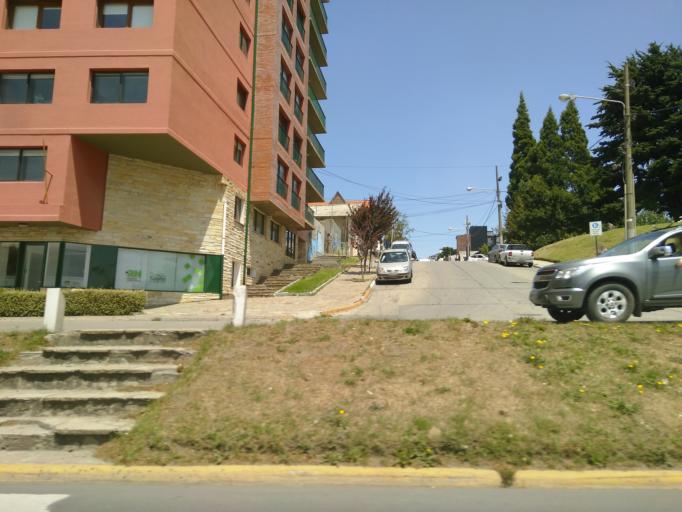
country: AR
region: Rio Negro
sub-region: Departamento de Bariloche
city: San Carlos de Bariloche
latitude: -41.1323
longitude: -71.3009
